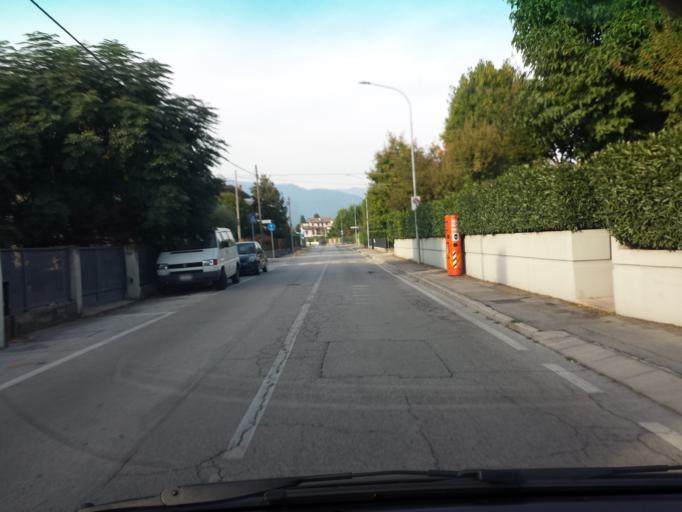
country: IT
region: Veneto
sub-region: Provincia di Vicenza
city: Nove
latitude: 45.7220
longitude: 11.6809
